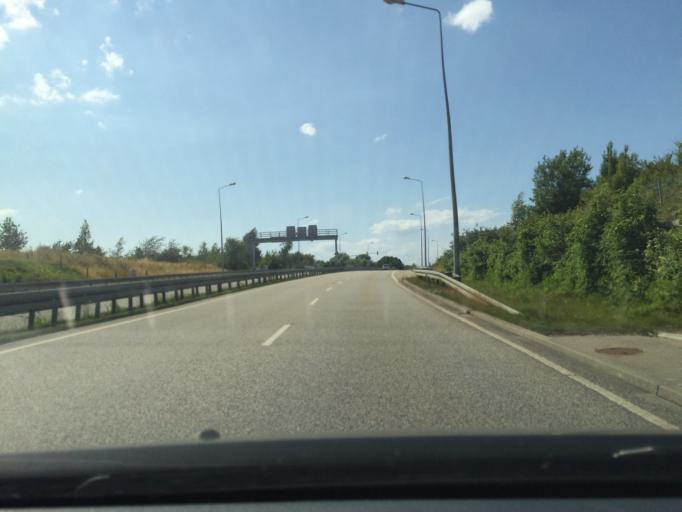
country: DE
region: Mecklenburg-Vorpommern
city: Warnemuende
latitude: 54.1350
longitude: 12.0862
